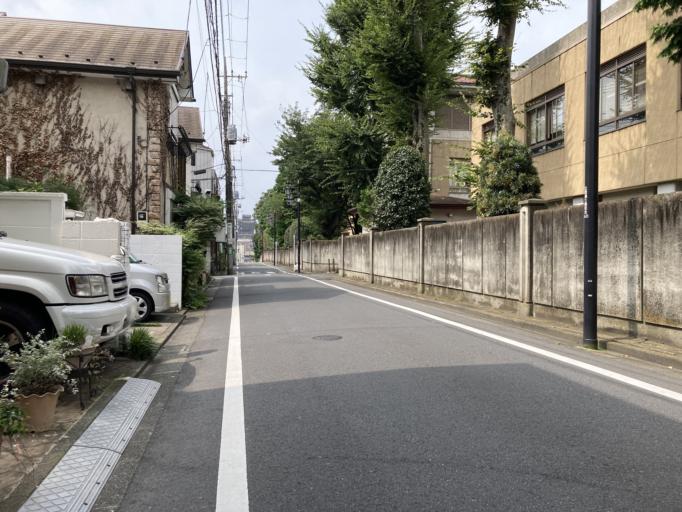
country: JP
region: Tokyo
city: Mitaka-shi
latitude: 35.6939
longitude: 139.5900
